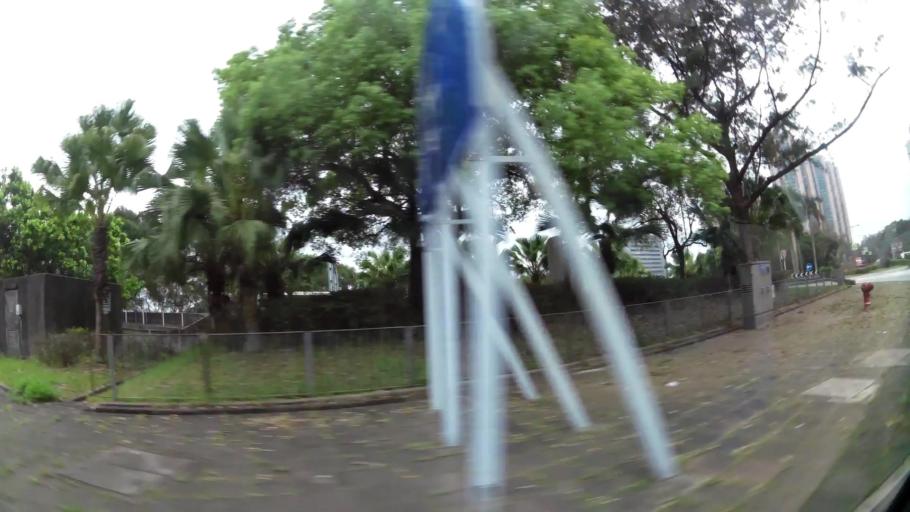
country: HK
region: Tsuen Wan
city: Tsuen Wan
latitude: 22.3473
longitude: 114.1105
